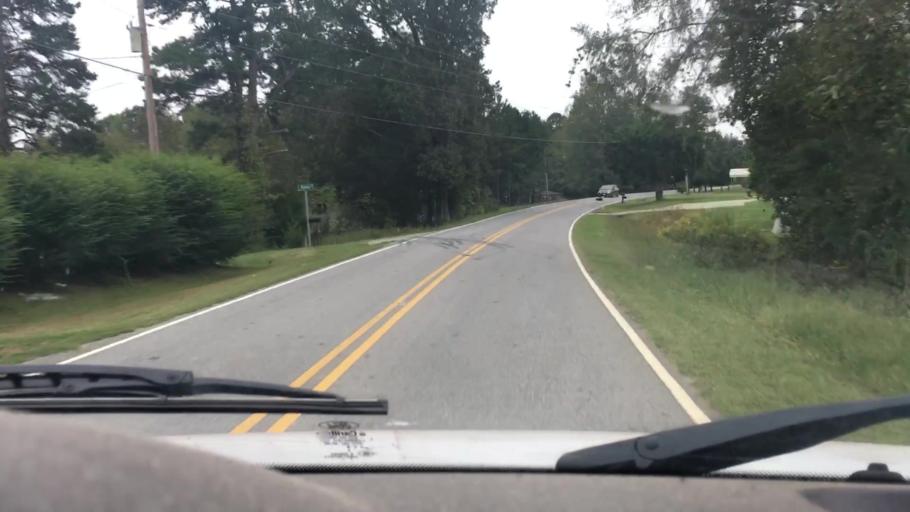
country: US
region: North Carolina
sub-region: Lincoln County
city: Westport
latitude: 35.4889
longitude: -81.0187
